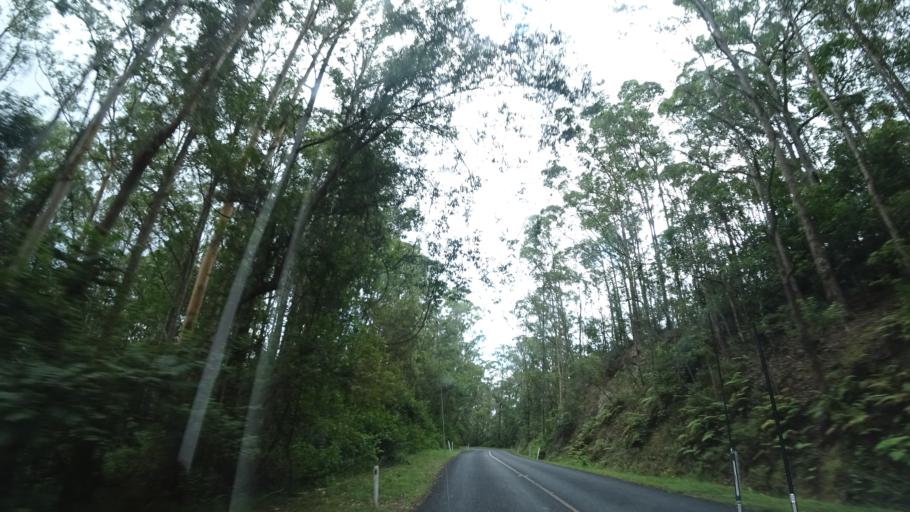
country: AU
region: Queensland
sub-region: Moreton Bay
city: Highvale
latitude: -27.3505
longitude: 152.7703
